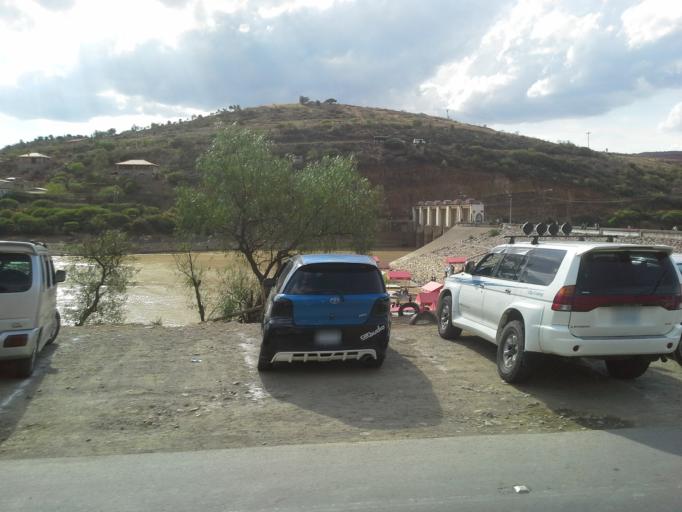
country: BO
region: Cochabamba
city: Tarata
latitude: -17.5288
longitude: -66.0848
